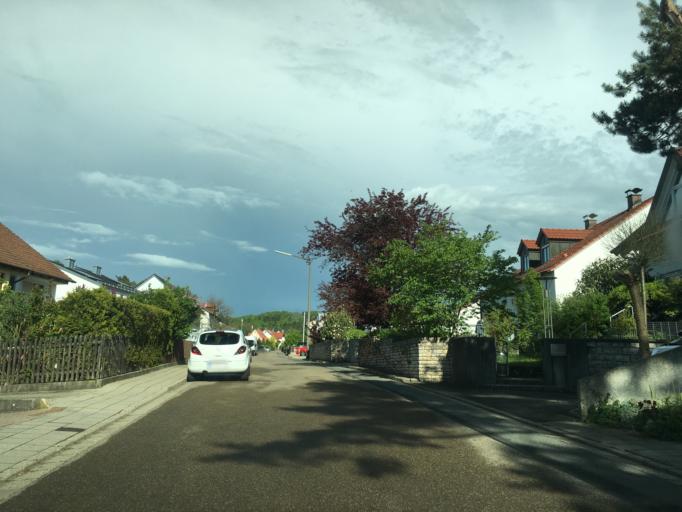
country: DE
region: Bavaria
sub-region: Upper Palatinate
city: Neumarkt in der Oberpfalz
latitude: 49.2854
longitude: 11.4826
